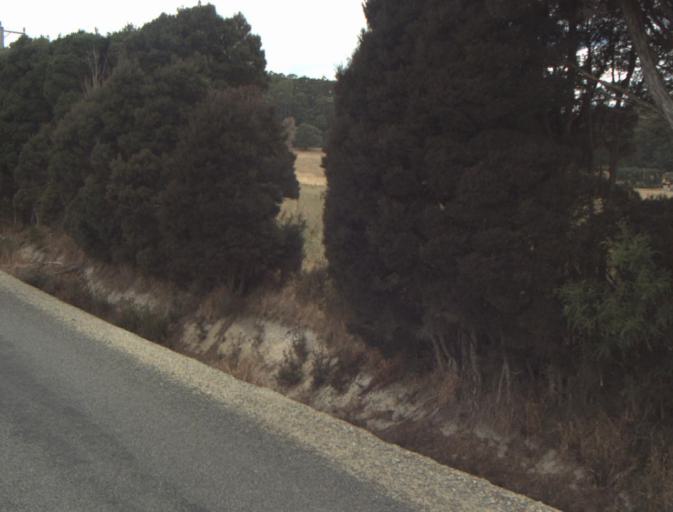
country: AU
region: Tasmania
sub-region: Launceston
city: Mayfield
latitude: -41.2047
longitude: 147.1886
